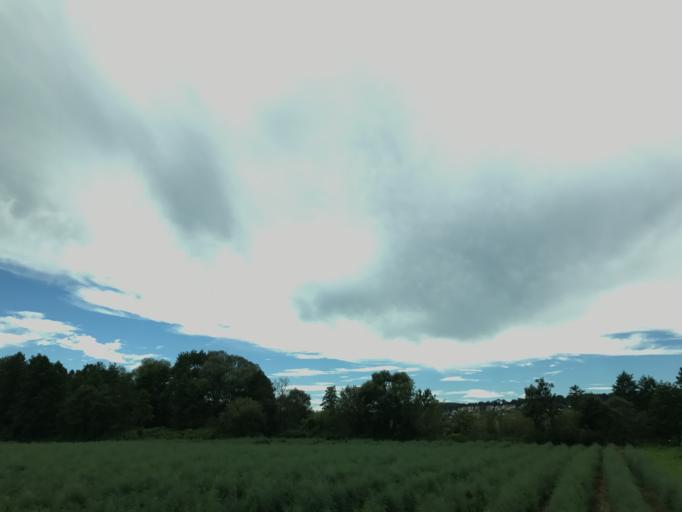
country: DE
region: Baden-Wuerttemberg
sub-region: Tuebingen Region
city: Berg
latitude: 47.8381
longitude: 9.6104
